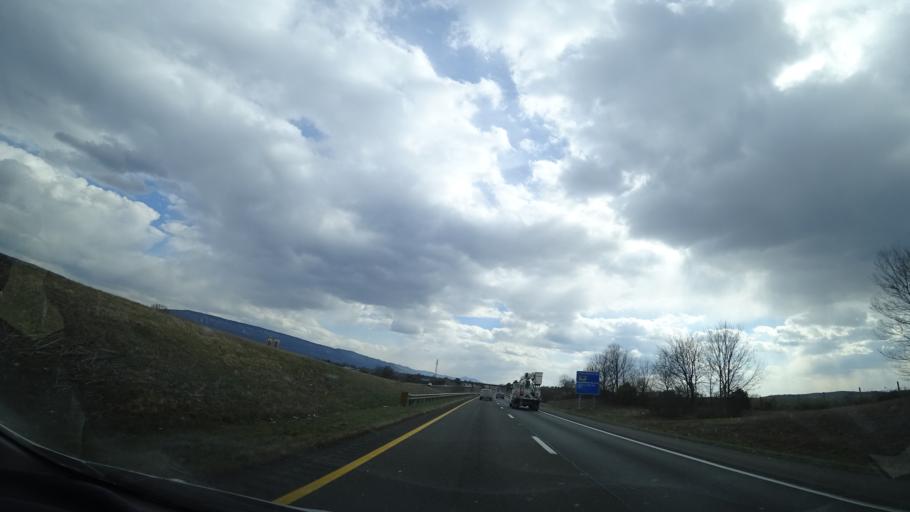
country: US
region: Virginia
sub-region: Shenandoah County
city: New Market
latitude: 38.6881
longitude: -78.6567
